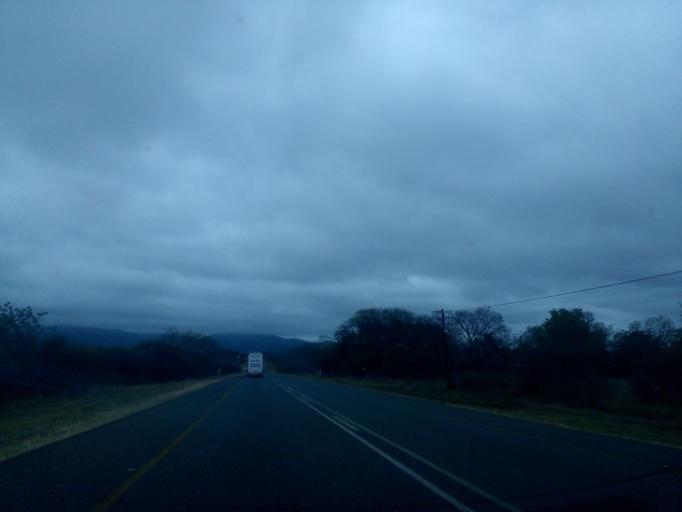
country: ZA
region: Limpopo
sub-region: Vhembe District Municipality
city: Louis Trichardt
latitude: -23.0881
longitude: 29.9054
